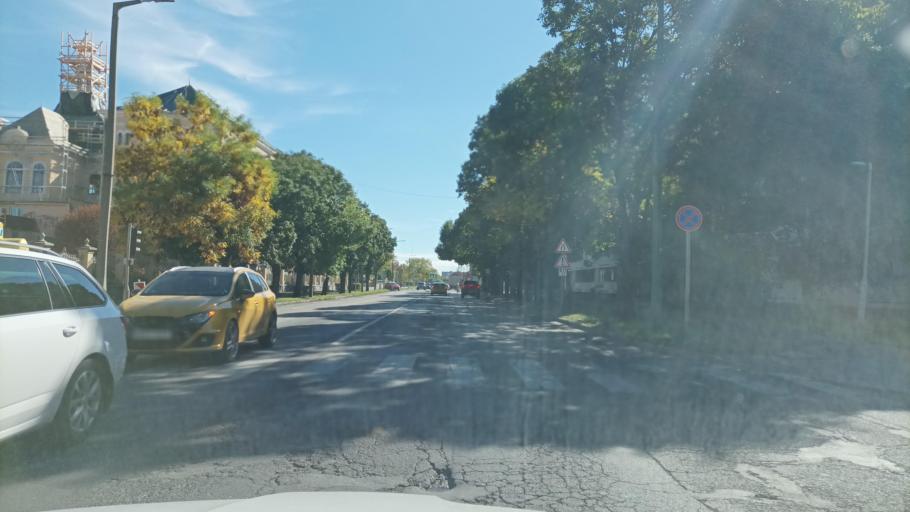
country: HU
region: Pest
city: Cegled
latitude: 47.1765
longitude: 19.8001
